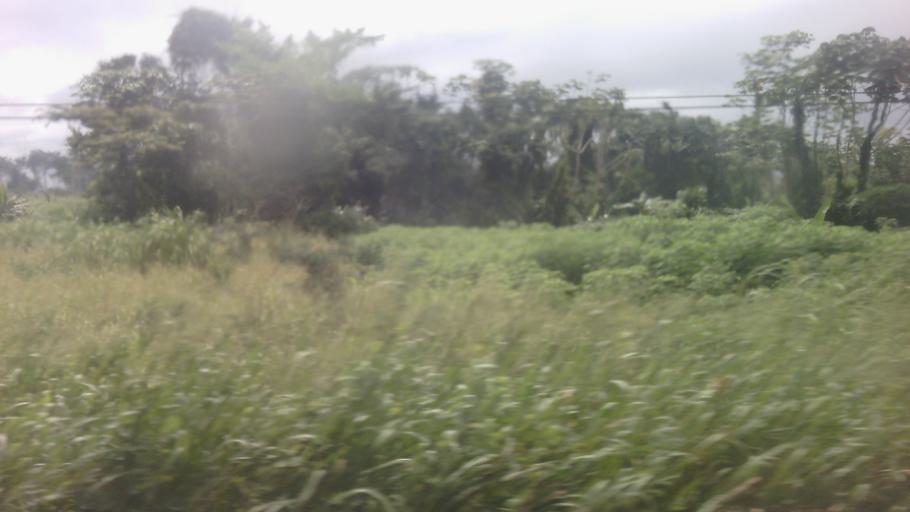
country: CI
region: Sud-Comoe
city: Aboisso
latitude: 5.4397
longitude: -3.2645
